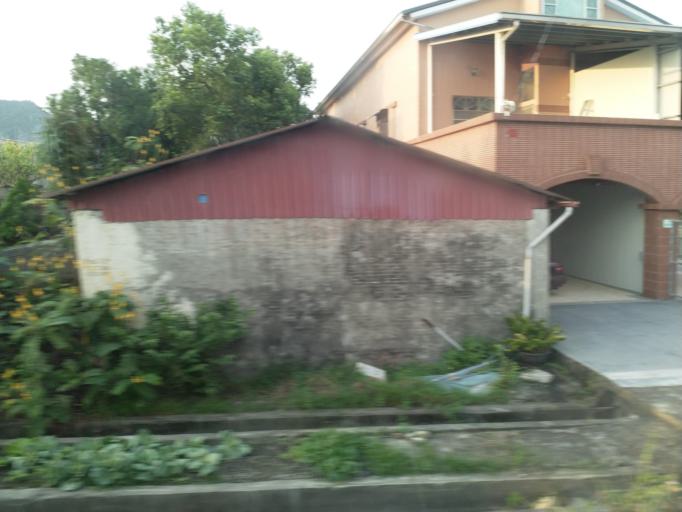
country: TW
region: Taiwan
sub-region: Pingtung
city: Pingtung
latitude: 22.8861
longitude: 120.5146
